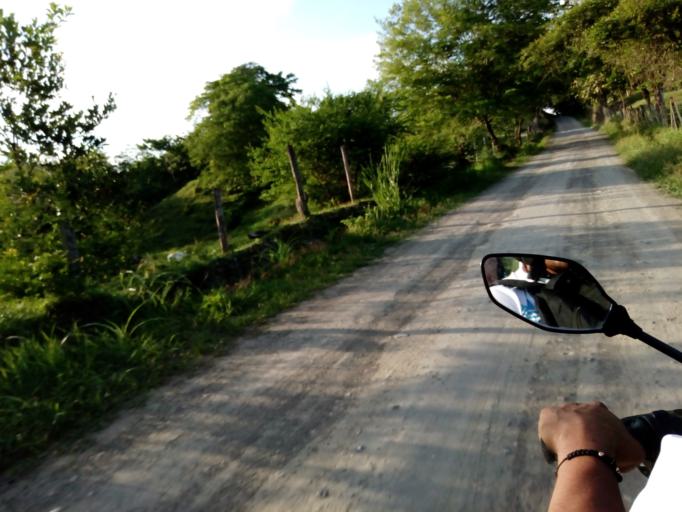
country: CO
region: Boyaca
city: Puerto Boyaca
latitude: 5.9607
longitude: -74.5899
